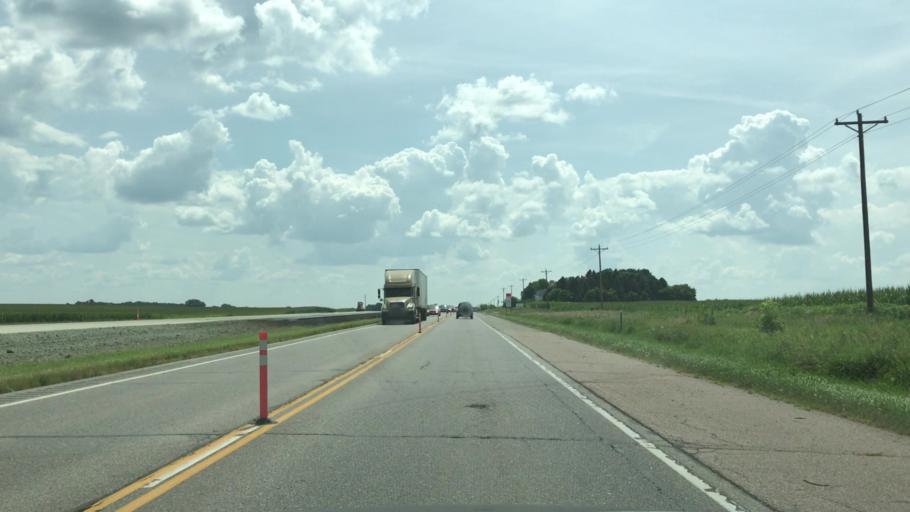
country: US
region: Minnesota
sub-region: Scott County
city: Belle Plaine
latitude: 44.5789
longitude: -93.8375
